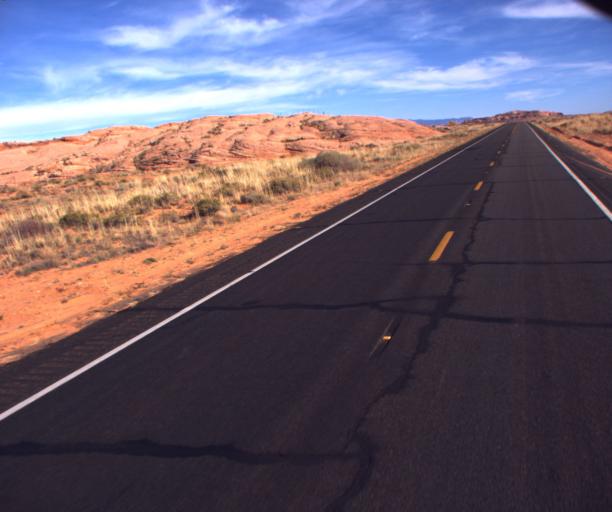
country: US
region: Arizona
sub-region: Apache County
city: Many Farms
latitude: 36.9350
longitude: -109.6324
